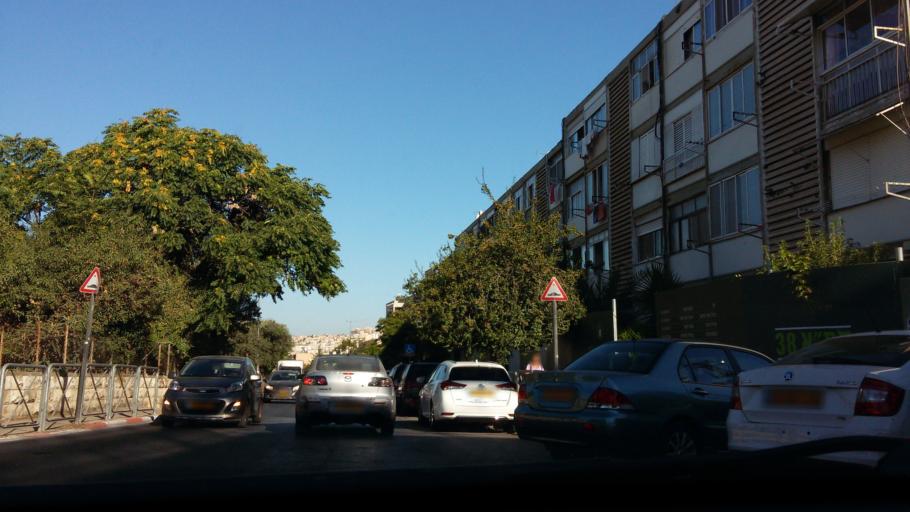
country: IL
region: Jerusalem
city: Jerusalem
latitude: 31.7549
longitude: 35.2175
